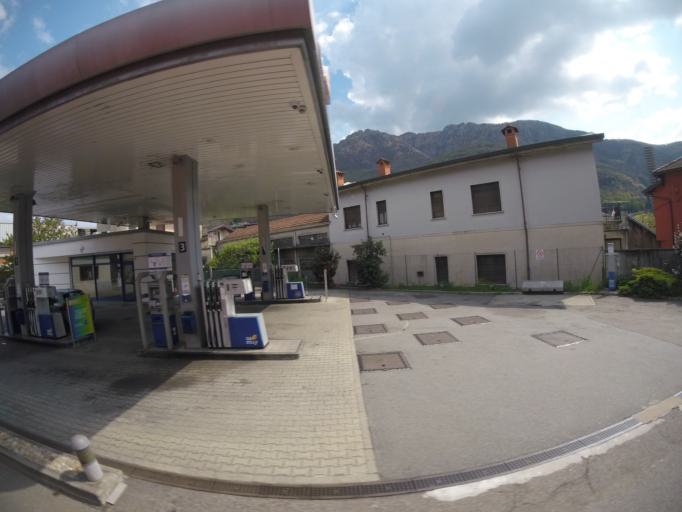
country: IT
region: Piedmont
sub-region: Provincia Verbano-Cusio-Ossola
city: Omegna
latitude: 45.8834
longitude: 8.4091
